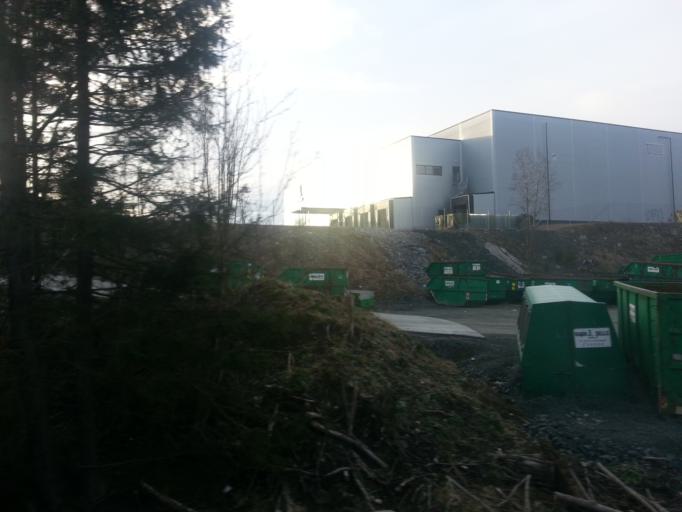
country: NO
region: Sor-Trondelag
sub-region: Melhus
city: Melhus
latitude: 63.3446
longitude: 10.3511
